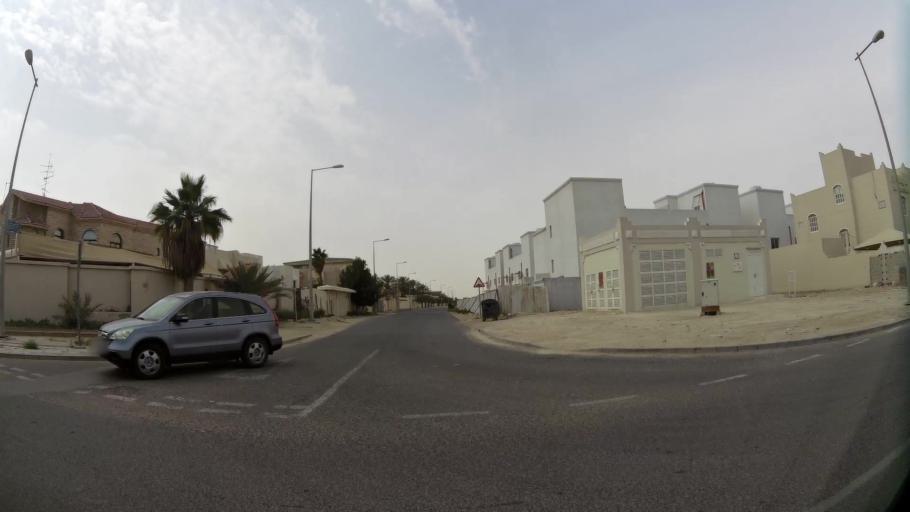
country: QA
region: Baladiyat ad Dawhah
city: Doha
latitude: 25.2674
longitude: 51.4931
